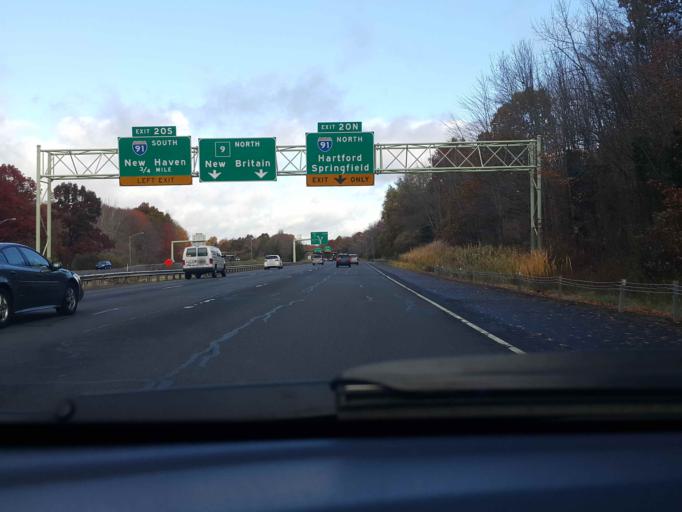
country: US
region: Connecticut
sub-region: Middlesex County
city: Cromwell
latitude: 41.6169
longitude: -72.6809
